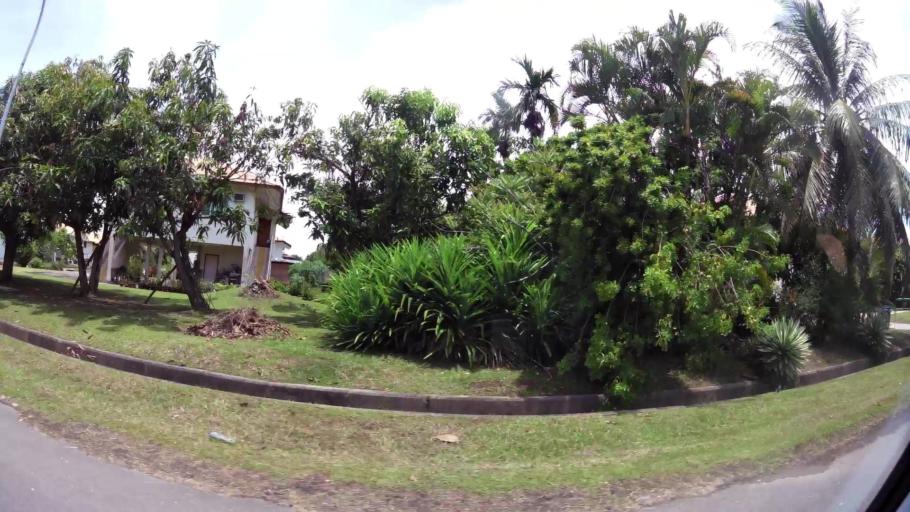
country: BN
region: Belait
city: Kuala Belait
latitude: 4.5885
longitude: 114.2469
